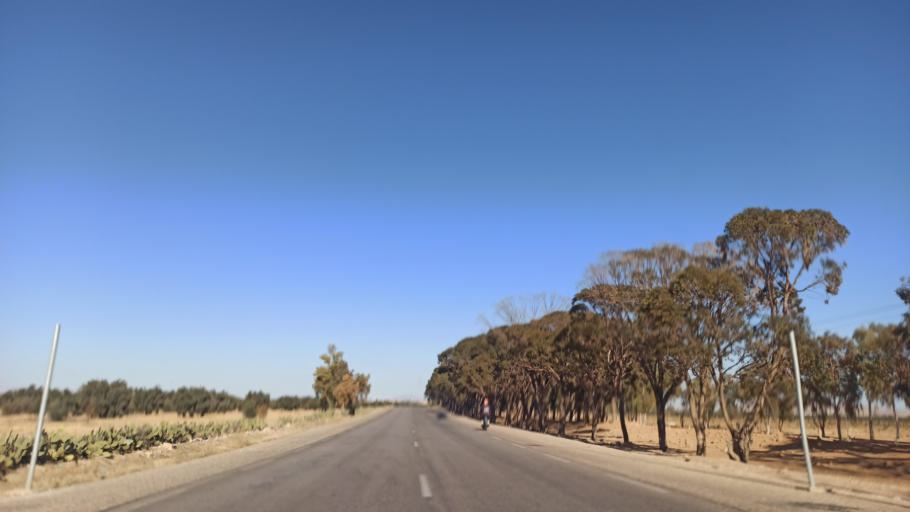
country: TN
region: Sidi Bu Zayd
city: Jilma
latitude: 35.2387
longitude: 9.3893
